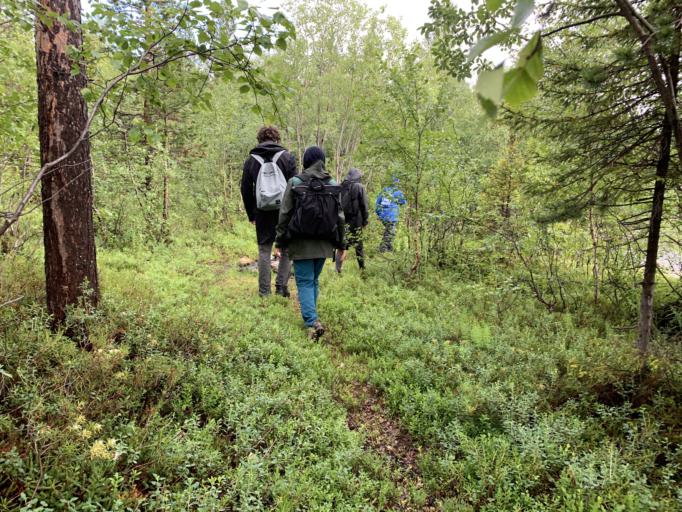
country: RU
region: Murmansk
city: Monchegorsk
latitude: 67.9394
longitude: 33.0392
